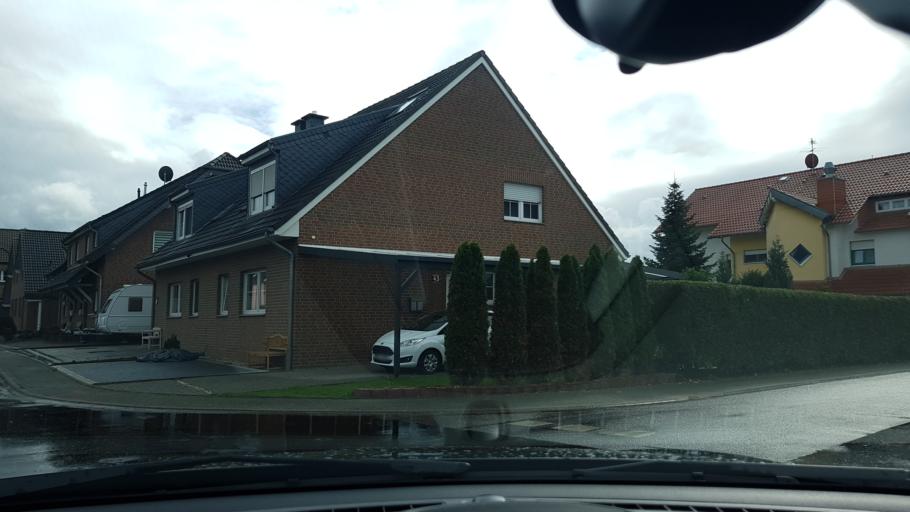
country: DE
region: North Rhine-Westphalia
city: Huckelhoven
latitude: 51.0592
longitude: 6.1966
